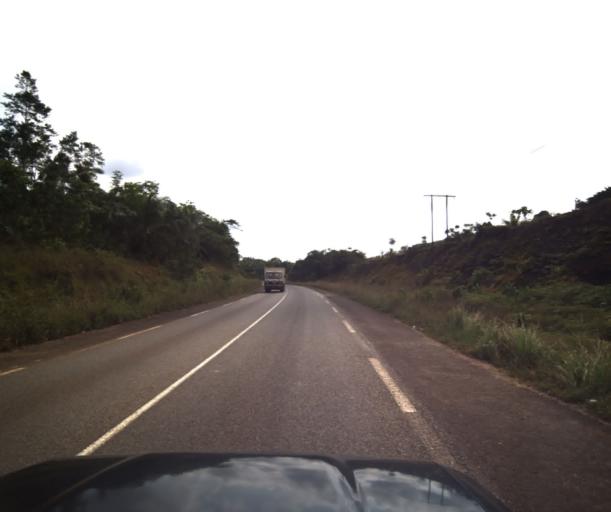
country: CM
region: Littoral
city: Edea
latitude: 3.7752
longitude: 10.1966
